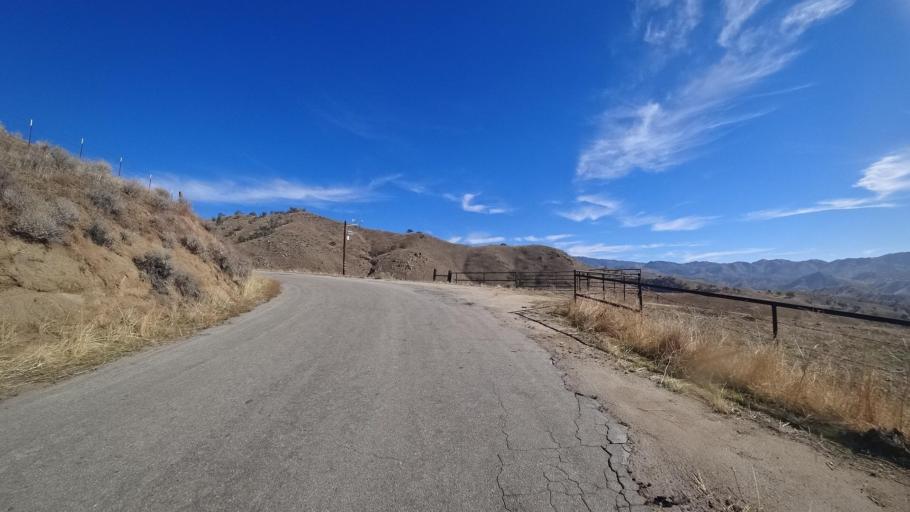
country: US
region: California
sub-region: Kern County
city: Arvin
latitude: 35.4248
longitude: -118.7303
